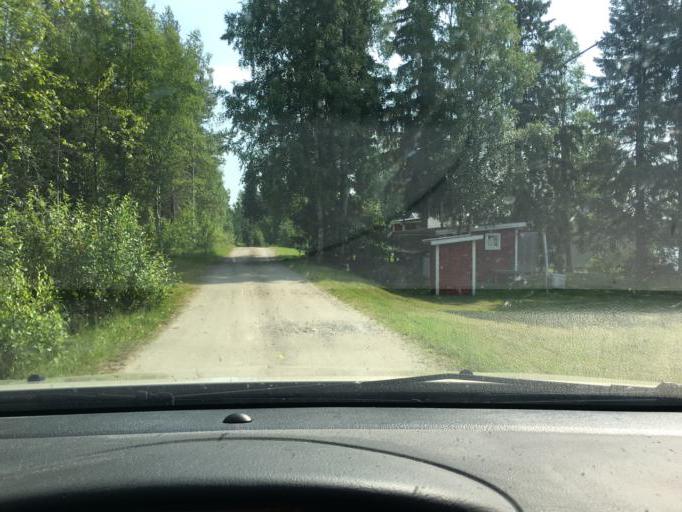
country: SE
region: Norrbotten
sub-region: Kalix Kommun
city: Rolfs
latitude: 65.7580
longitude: 22.9966
